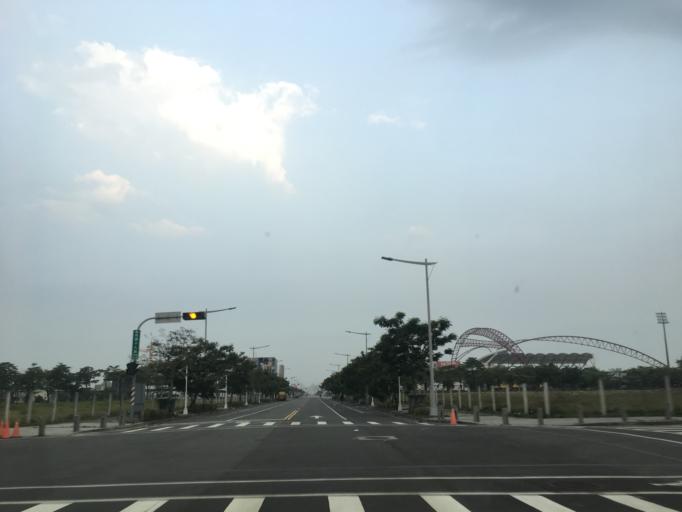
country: TW
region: Taiwan
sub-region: Taichung City
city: Taichung
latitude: 24.1979
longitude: 120.6889
